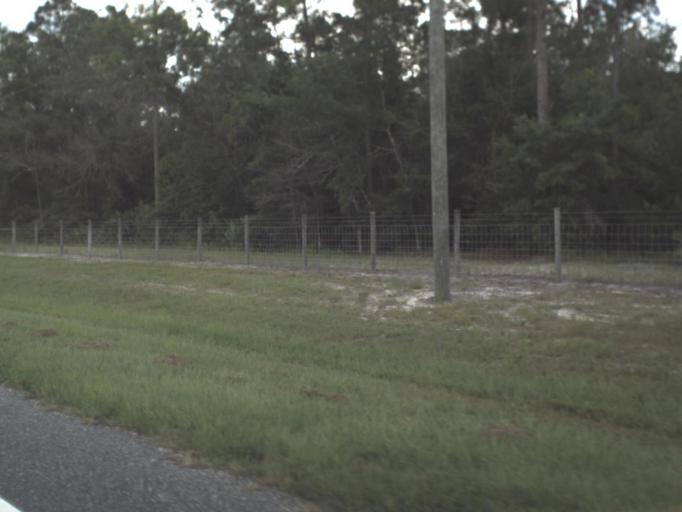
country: US
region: Florida
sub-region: Clay County
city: Middleburg
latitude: 29.9818
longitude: -81.9376
